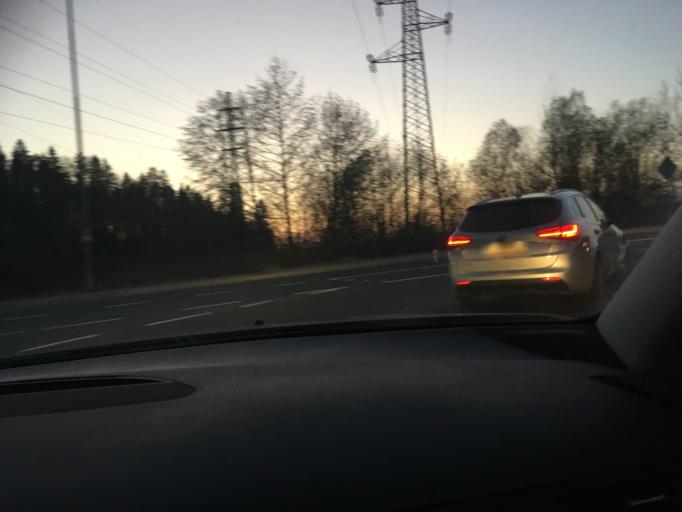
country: SI
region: Domzale
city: Vir
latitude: 46.1334
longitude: 14.6160
